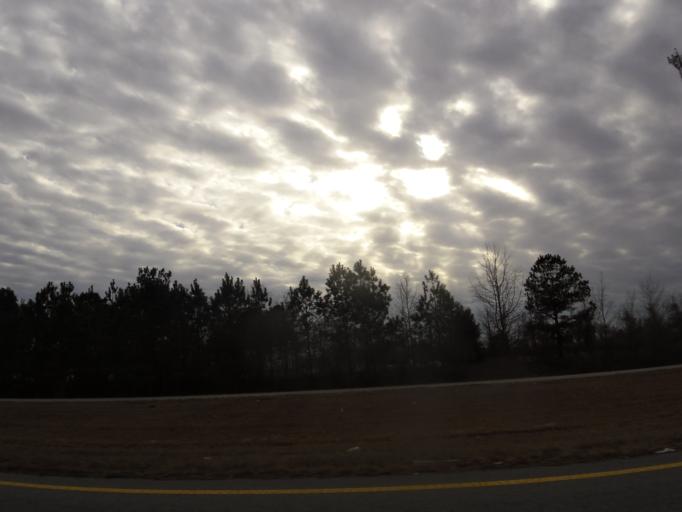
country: US
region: North Carolina
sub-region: Hertford County
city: Murfreesboro
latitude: 36.4322
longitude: -77.1298
